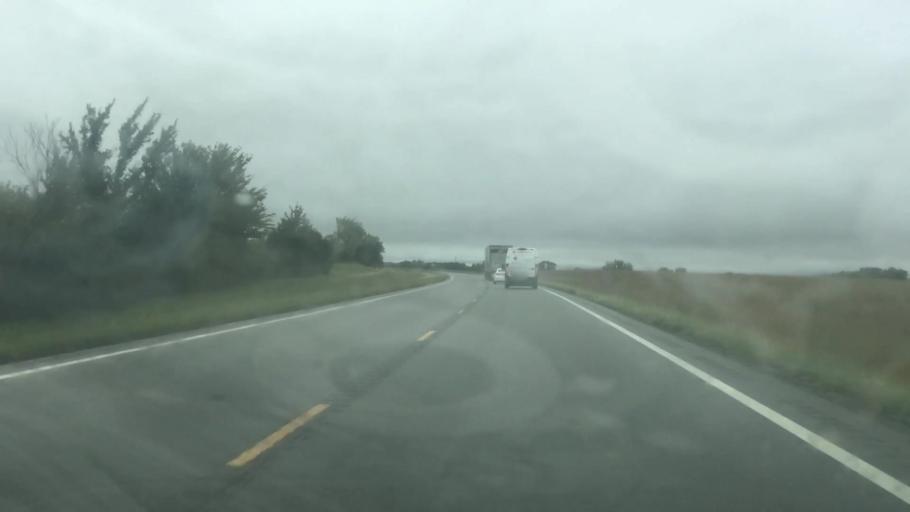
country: US
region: Kansas
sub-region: Anderson County
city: Garnett
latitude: 38.1442
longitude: -95.3268
